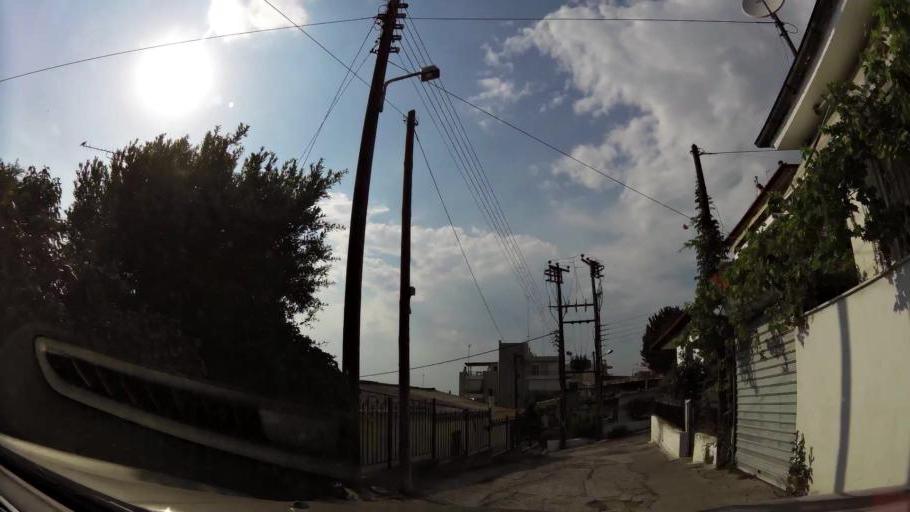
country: GR
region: Central Macedonia
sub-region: Nomos Thessalonikis
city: Polichni
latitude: 40.6599
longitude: 22.9596
